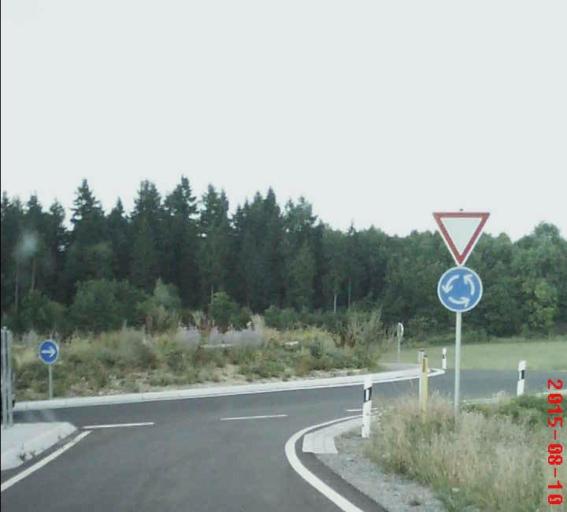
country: DE
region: Thuringia
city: Ellingshausen
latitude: 50.5710
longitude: 10.4478
